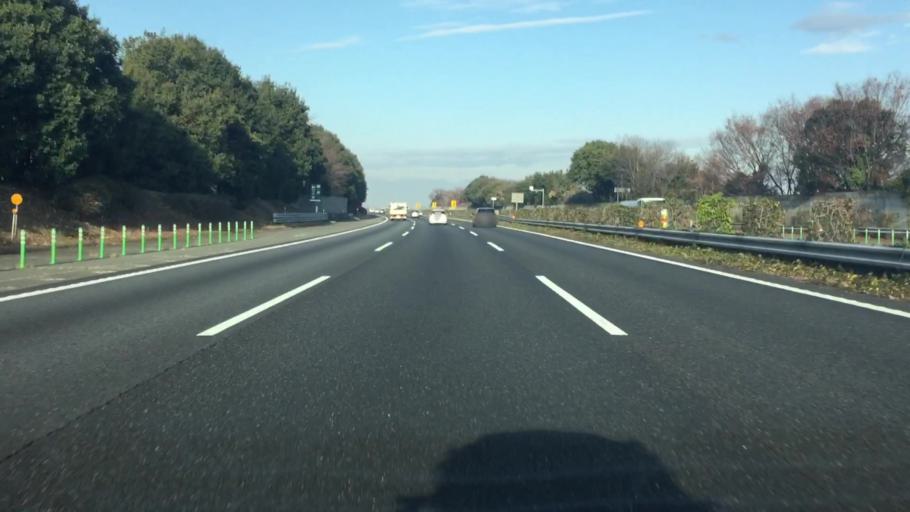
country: JP
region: Saitama
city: Honjo
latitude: 36.2464
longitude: 139.1407
